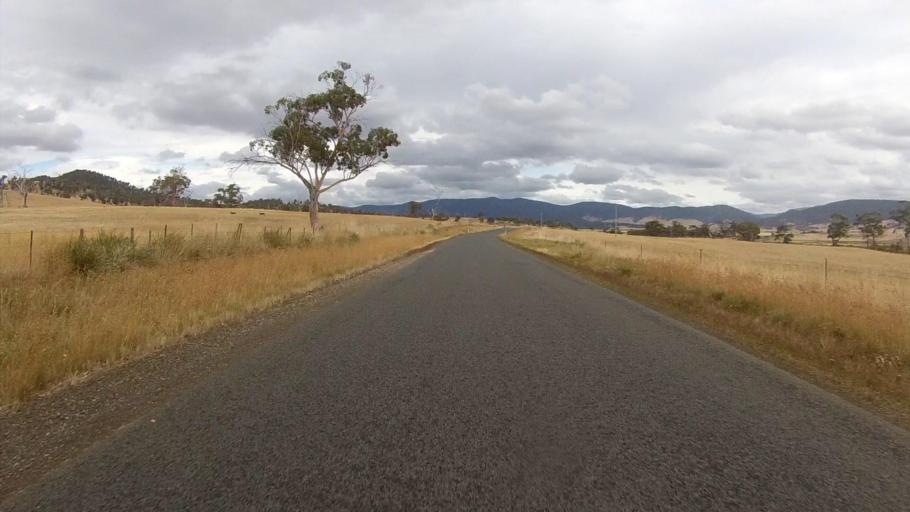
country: AU
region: Tasmania
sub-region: Northern Midlands
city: Evandale
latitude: -41.7991
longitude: 147.7491
